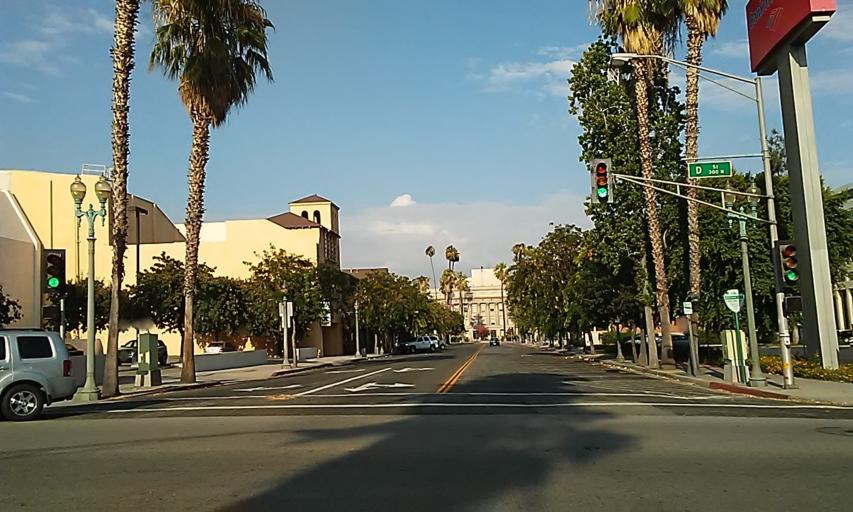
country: US
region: California
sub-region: San Bernardino County
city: San Bernardino
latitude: 34.1055
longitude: -117.2920
